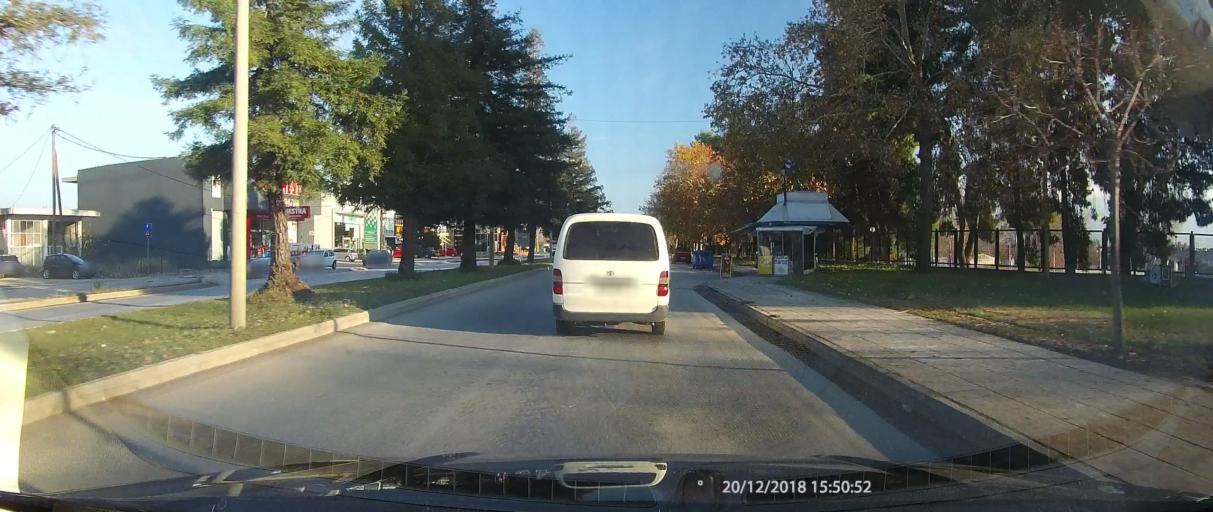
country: GR
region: Central Greece
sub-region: Nomos Fthiotidos
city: Lamia
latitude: 38.8928
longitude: 22.4481
